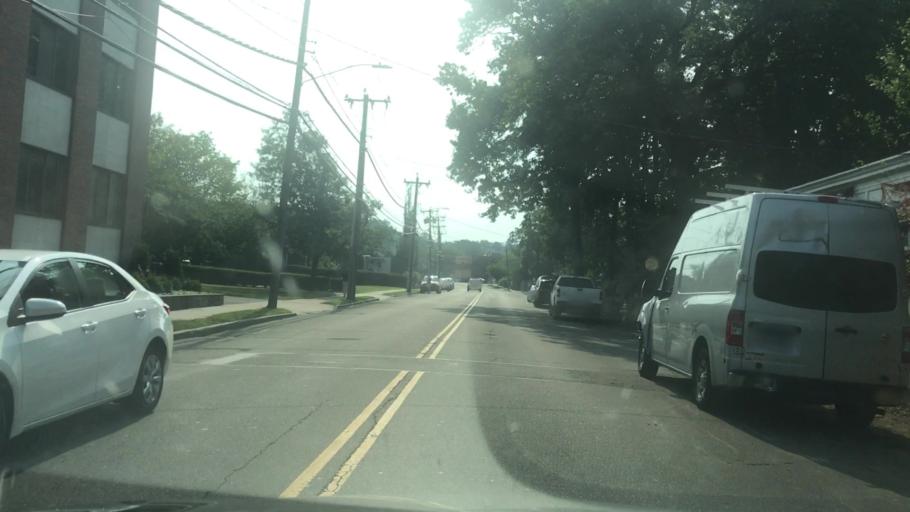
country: US
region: Connecticut
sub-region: Fairfield County
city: Greenwich
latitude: 41.0215
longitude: -73.6290
